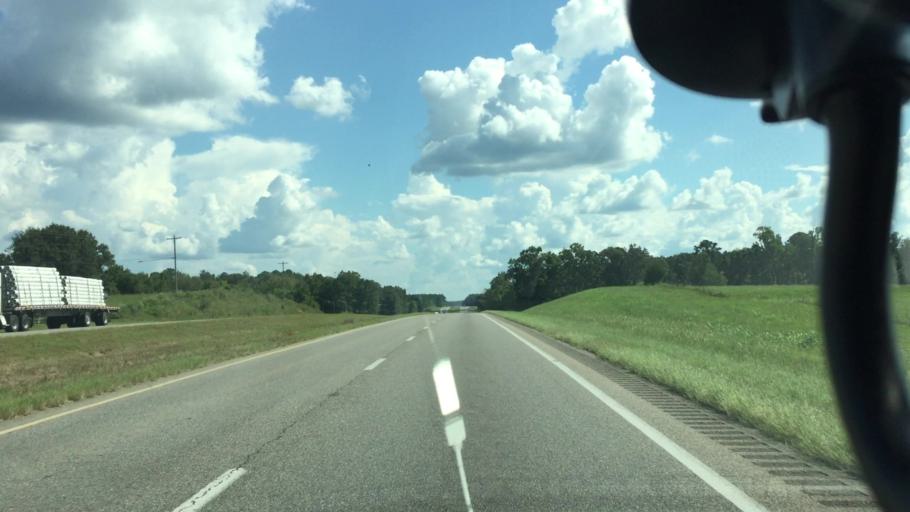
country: US
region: Alabama
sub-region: Montgomery County
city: Pike Road
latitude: 32.2173
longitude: -86.1180
